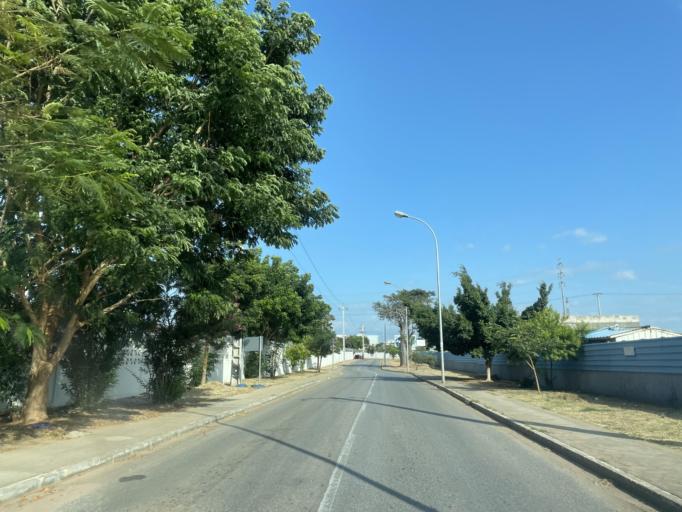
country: AO
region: Luanda
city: Luanda
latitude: -8.9154
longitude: 13.1898
